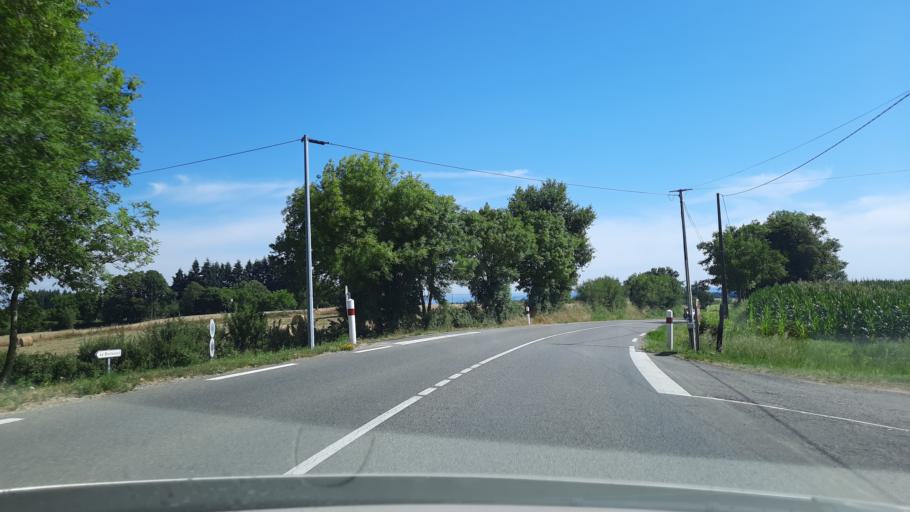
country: FR
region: Midi-Pyrenees
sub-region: Departement de l'Aveyron
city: Montbazens
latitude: 44.4413
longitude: 2.1955
